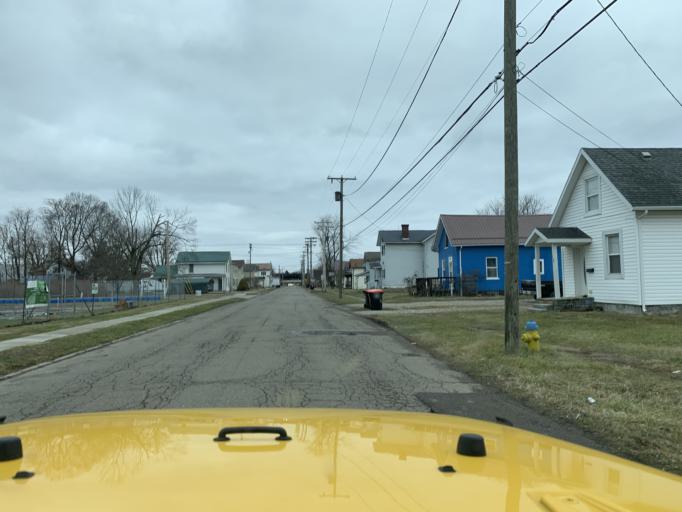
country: US
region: Ohio
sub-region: Licking County
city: Newark
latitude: 40.0505
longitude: -82.4064
